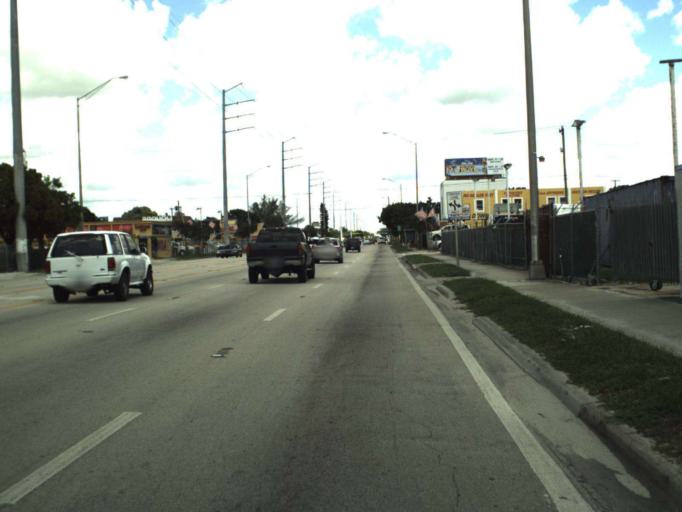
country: US
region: Florida
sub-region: Miami-Dade County
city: Pinewood
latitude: 25.8775
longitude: -80.2102
